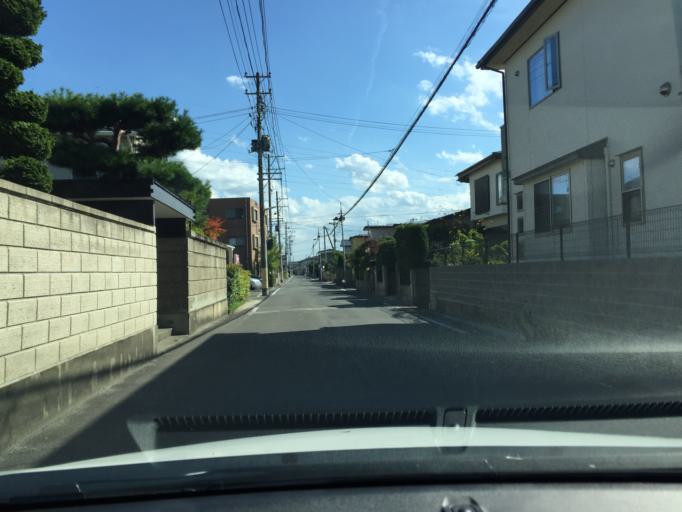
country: JP
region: Fukushima
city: Fukushima-shi
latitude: 37.7742
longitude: 140.4449
